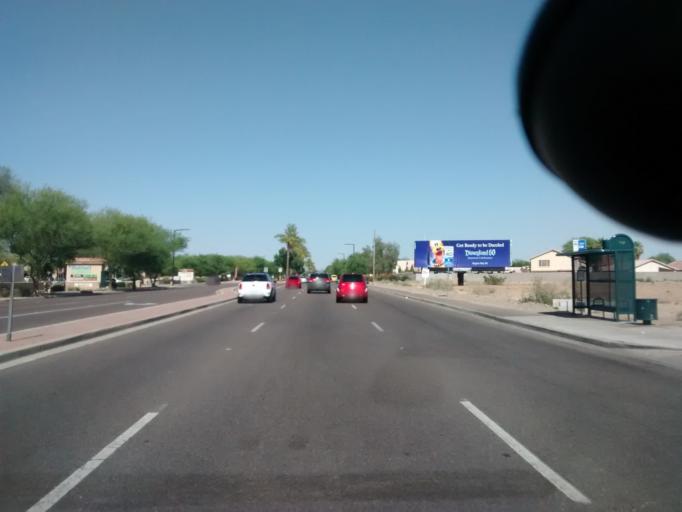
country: US
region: Arizona
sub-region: Maricopa County
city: Glendale
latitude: 33.5379
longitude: -112.2198
